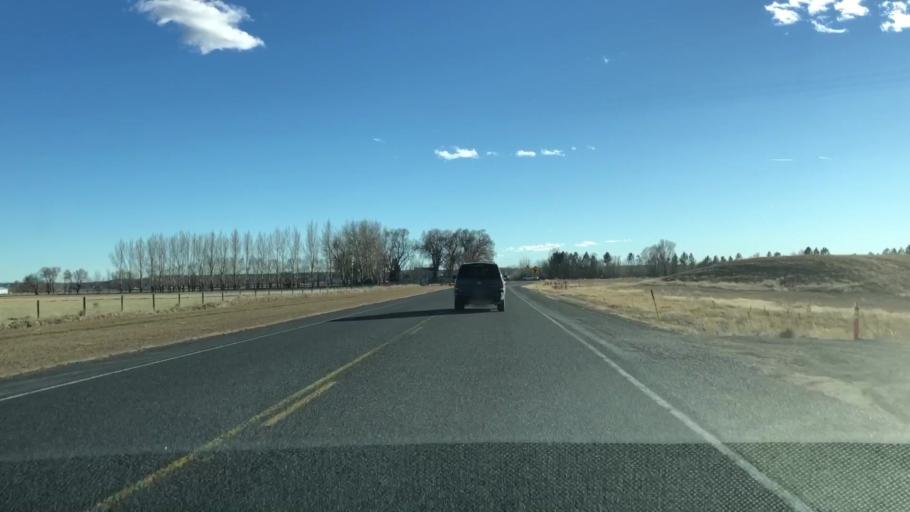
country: US
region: Colorado
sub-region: Weld County
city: Windsor
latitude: 40.5113
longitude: -104.9818
